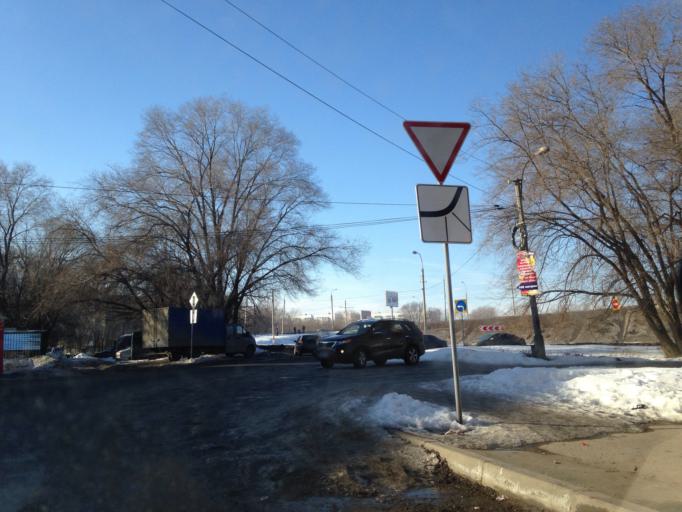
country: RU
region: Ulyanovsk
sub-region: Ulyanovskiy Rayon
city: Ulyanovsk
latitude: 54.2922
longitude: 48.3161
